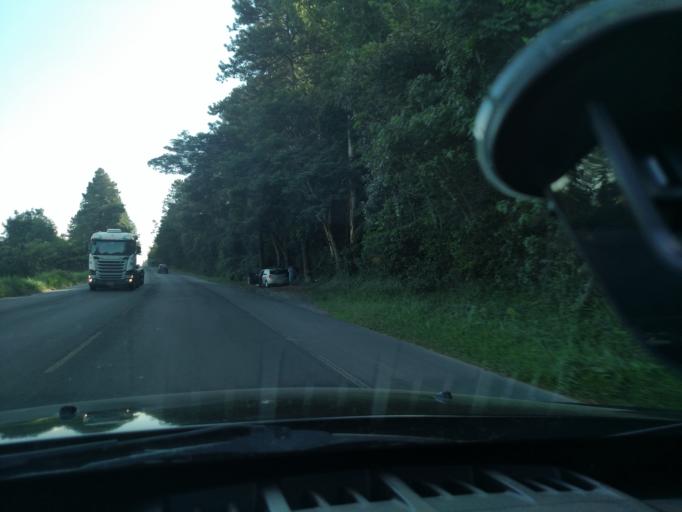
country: BR
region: Santa Catarina
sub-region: Rio Do Sul
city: Rio do Sul
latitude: -27.2645
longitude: -49.7256
